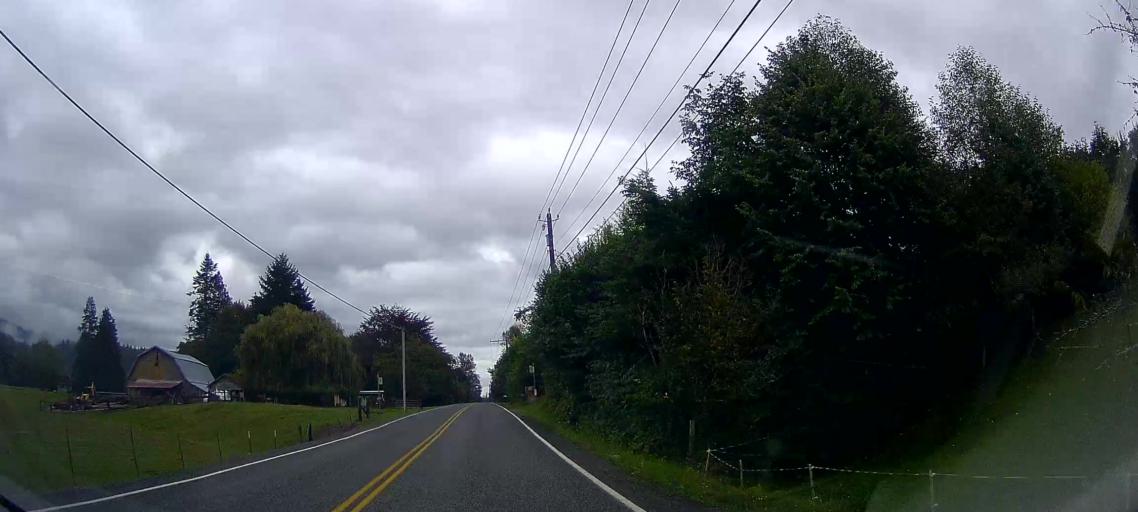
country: US
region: Washington
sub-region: Skagit County
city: Sedro-Woolley
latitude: 48.5265
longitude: -122.0985
